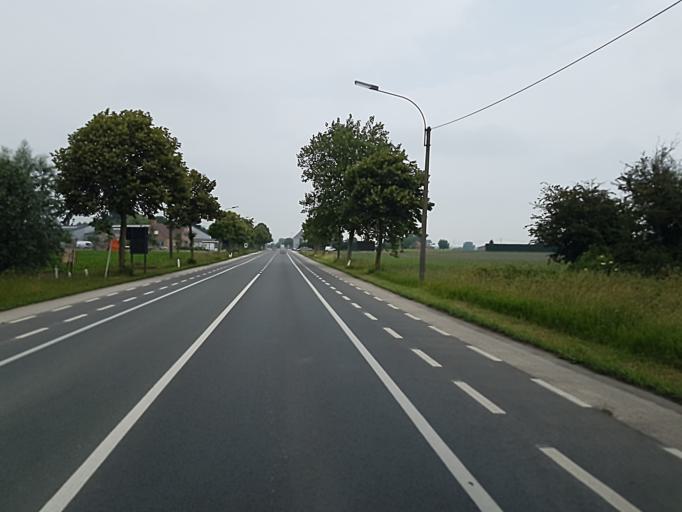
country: BE
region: Flanders
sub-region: Provincie West-Vlaanderen
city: Meulebeke
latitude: 50.9688
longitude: 3.3033
